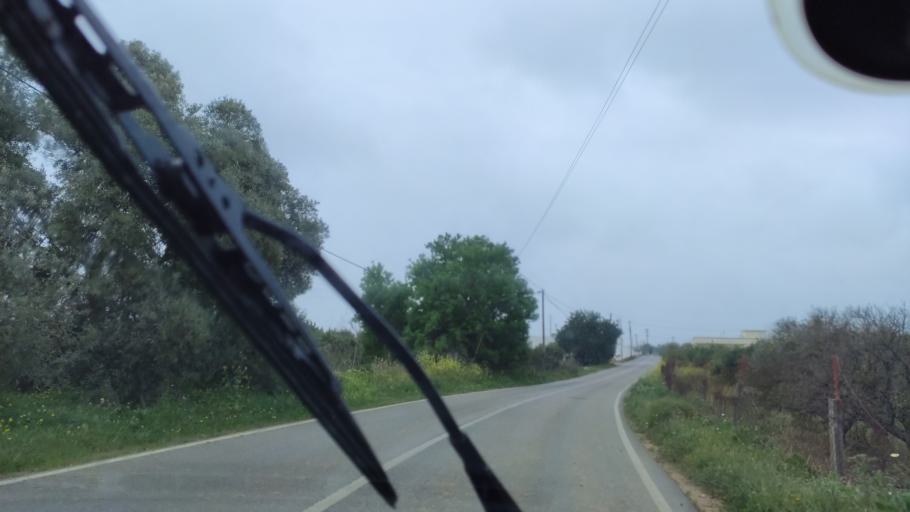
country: PT
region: Faro
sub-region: Faro
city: Santa Barbara de Nexe
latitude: 37.0737
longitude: -7.9467
